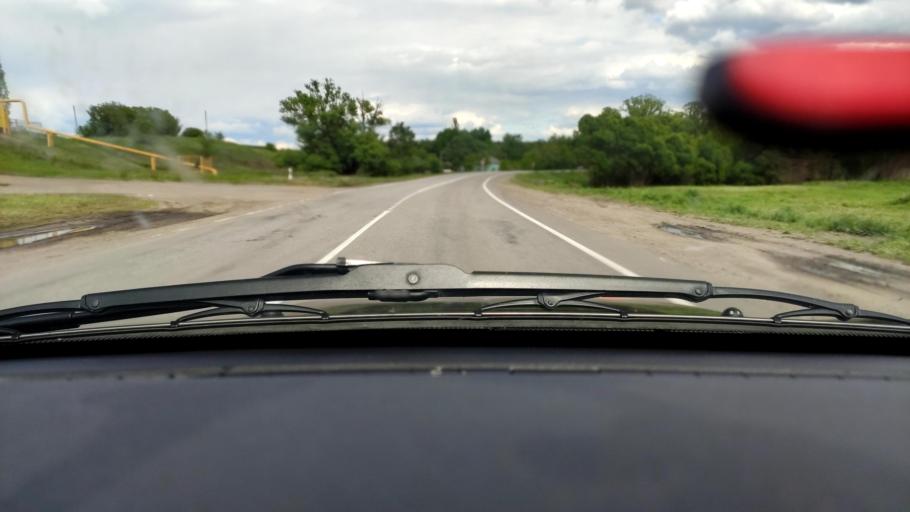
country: RU
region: Voronezj
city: Ostrogozhsk
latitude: 51.0551
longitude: 38.9182
